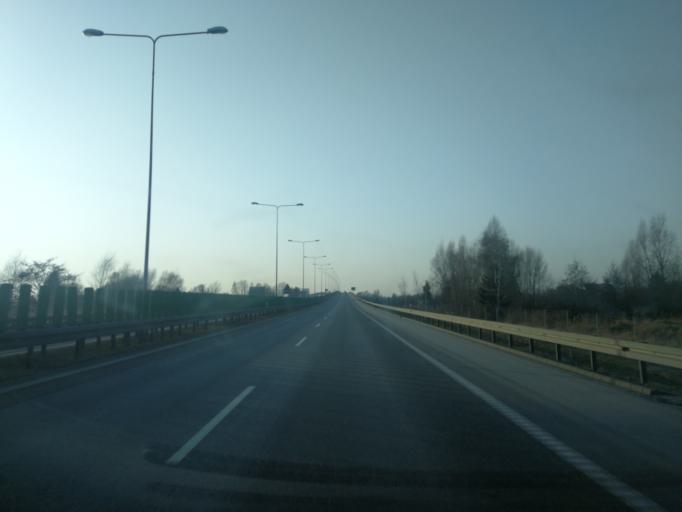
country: PL
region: Warmian-Masurian Voivodeship
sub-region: Powiat elblaski
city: Elblag
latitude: 54.1415
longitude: 19.4018
